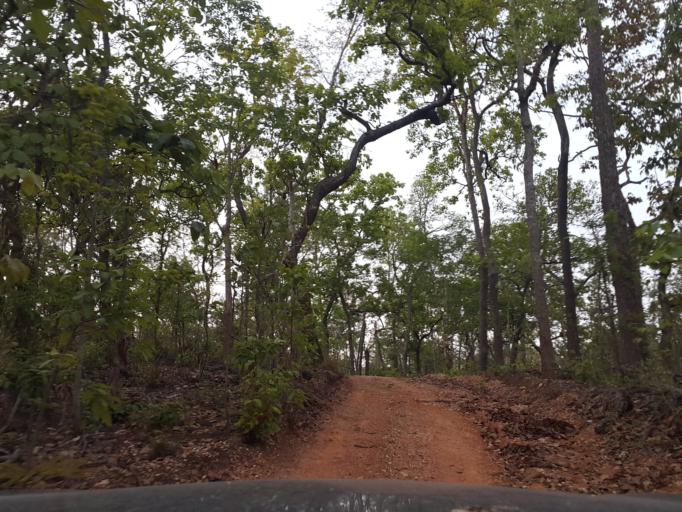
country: TH
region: Lamphun
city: Thung Hua Chang
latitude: 17.9112
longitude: 99.0790
